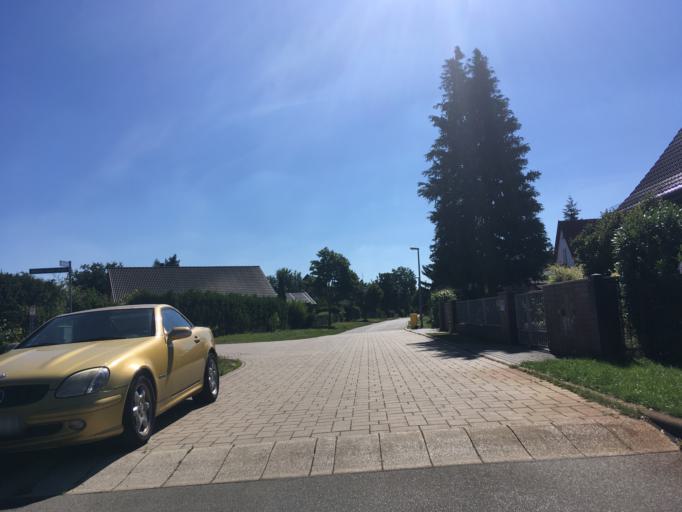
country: DE
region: Brandenburg
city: Altlandsberg
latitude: 52.5408
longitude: 13.7387
